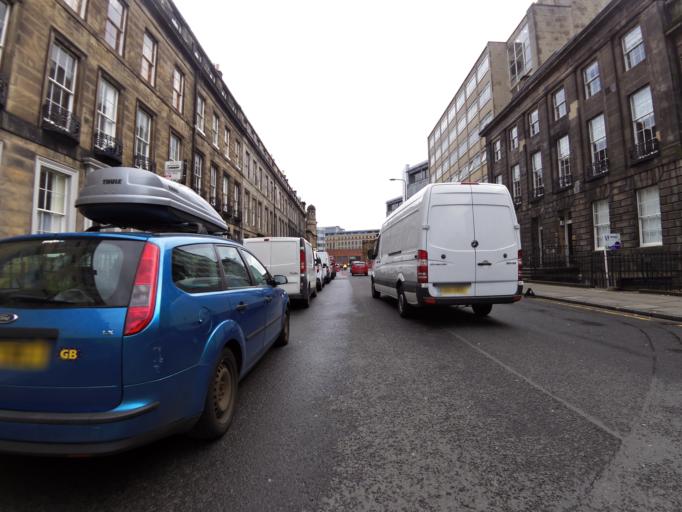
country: GB
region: Scotland
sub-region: Edinburgh
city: Edinburgh
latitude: 55.9470
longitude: -3.2137
